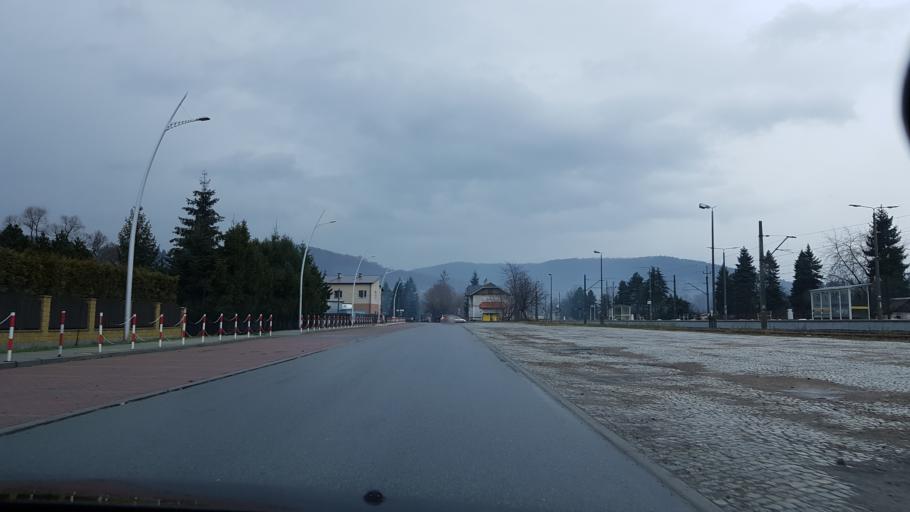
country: PL
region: Lesser Poland Voivodeship
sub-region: Powiat suski
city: Makow Podhalanski
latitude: 49.7274
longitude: 19.6754
